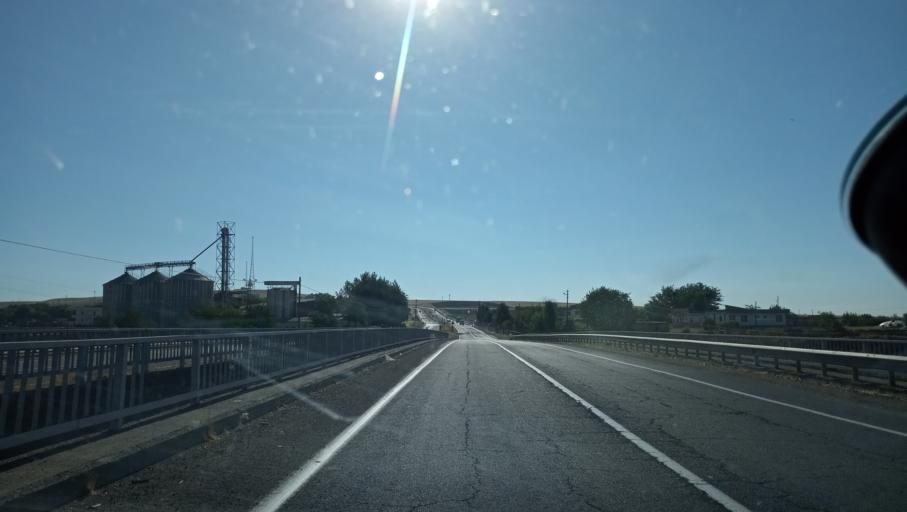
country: TR
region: Diyarbakir
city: Sur
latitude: 37.9909
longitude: 40.3826
